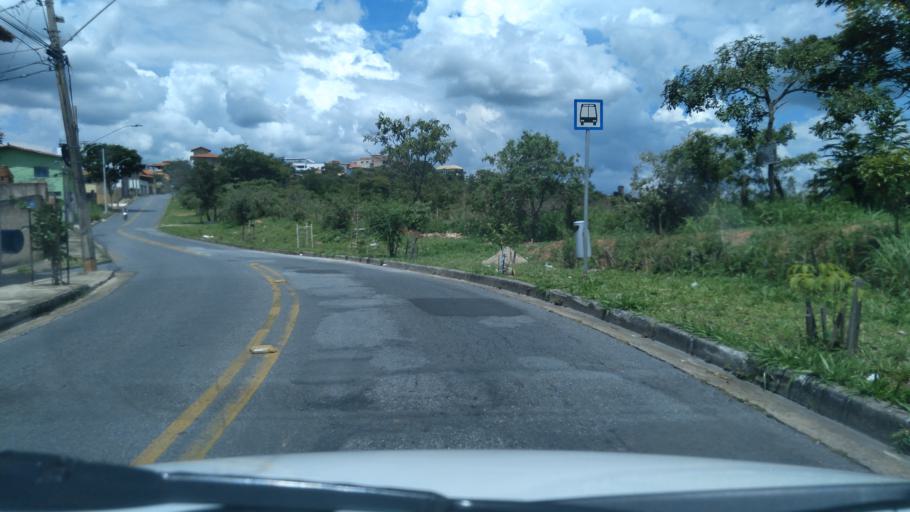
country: BR
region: Minas Gerais
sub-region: Belo Horizonte
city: Belo Horizonte
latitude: -19.8635
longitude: -43.8858
